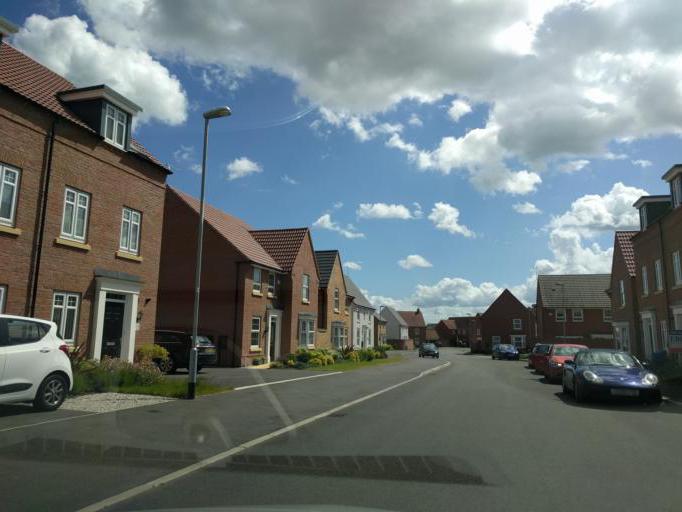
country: GB
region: England
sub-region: Nottinghamshire
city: Newark on Trent
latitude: 53.0496
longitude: -0.7671
